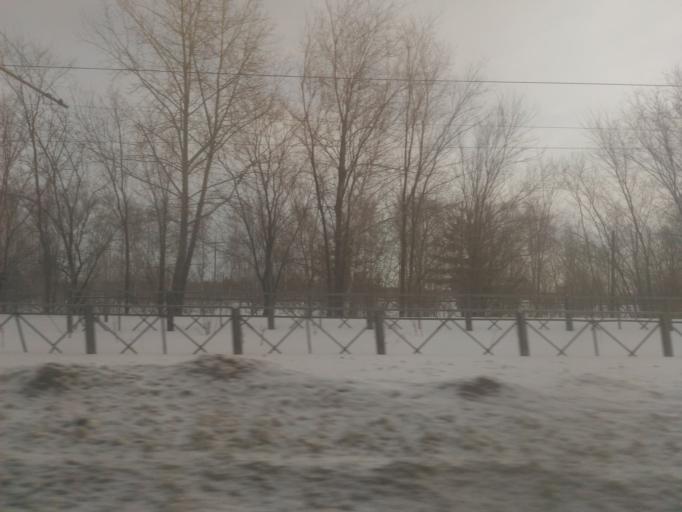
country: RU
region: Ulyanovsk
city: Isheyevka
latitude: 54.3686
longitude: 48.3166
